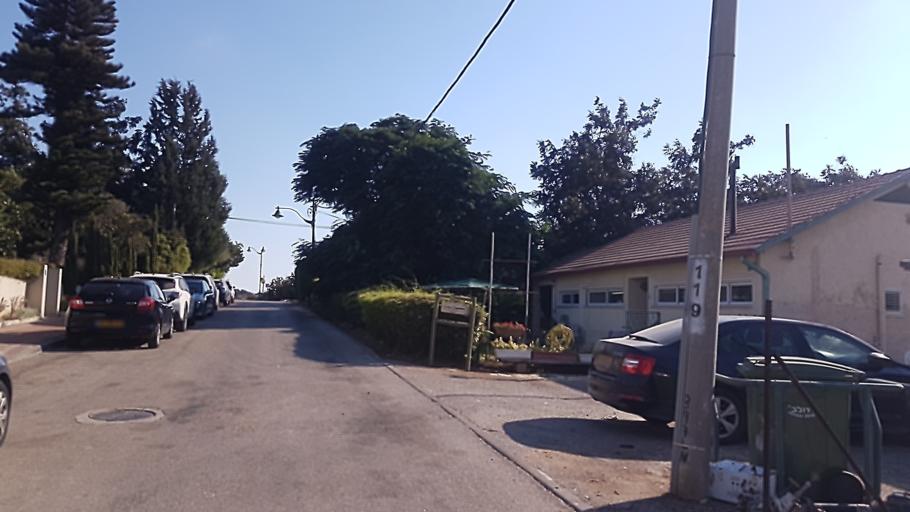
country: IL
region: Central District
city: Kfar Saba
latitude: 32.2038
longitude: 34.9052
